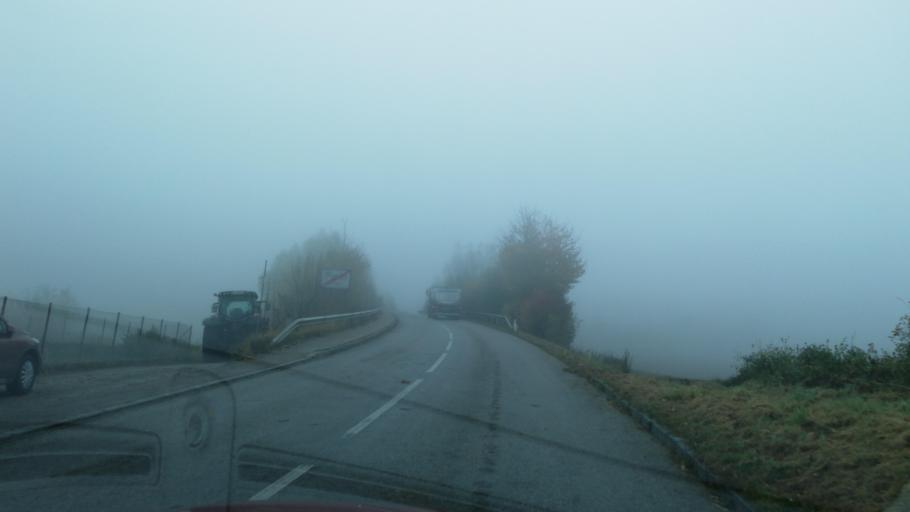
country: AT
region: Upper Austria
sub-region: Politischer Bezirk Grieskirchen
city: Bad Schallerbach
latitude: 48.1829
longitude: 13.9017
